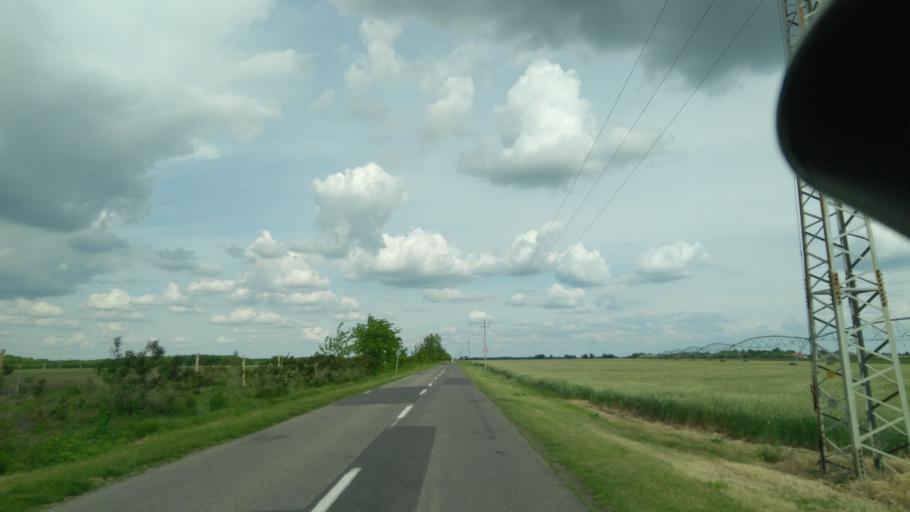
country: HU
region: Bekes
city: Mezohegyes
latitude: 46.3089
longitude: 20.8767
